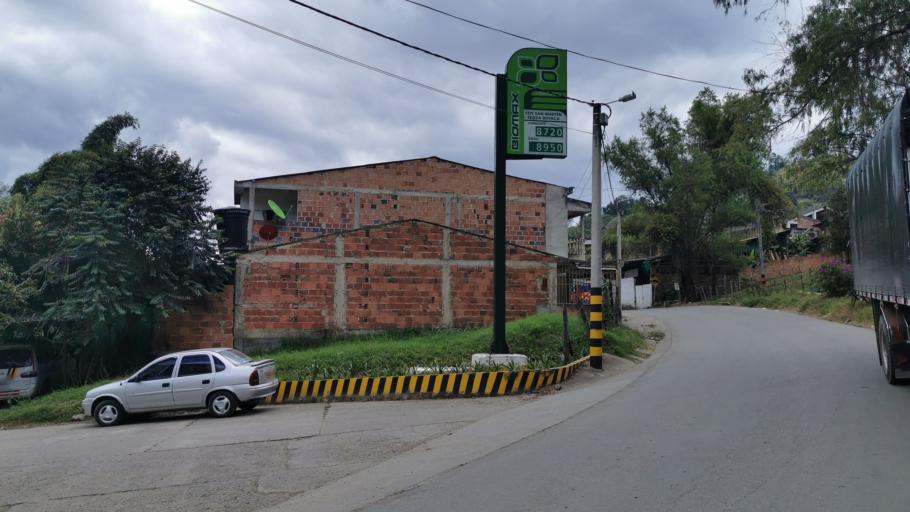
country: CO
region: Cundinamarca
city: Tenza
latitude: 5.0785
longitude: -73.4243
